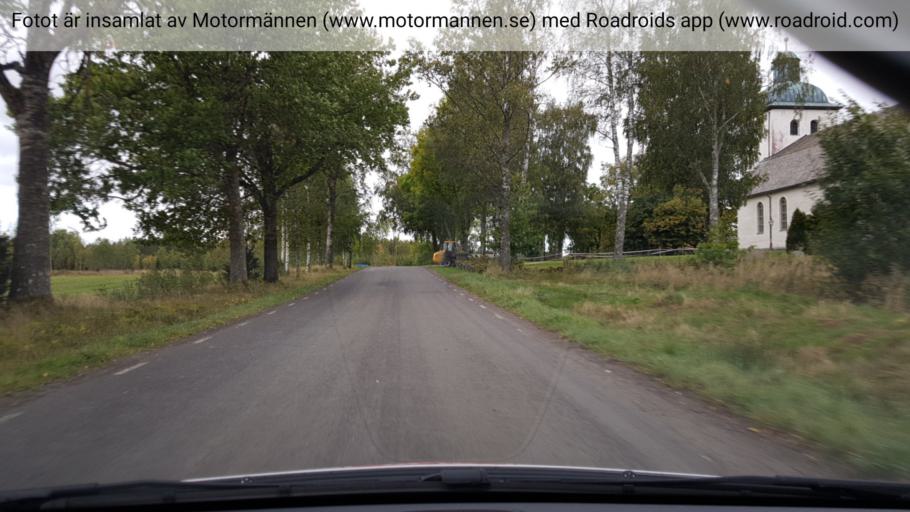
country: SE
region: Vaermland
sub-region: Saffle Kommun
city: Saeffle
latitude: 59.1326
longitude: 13.1060
